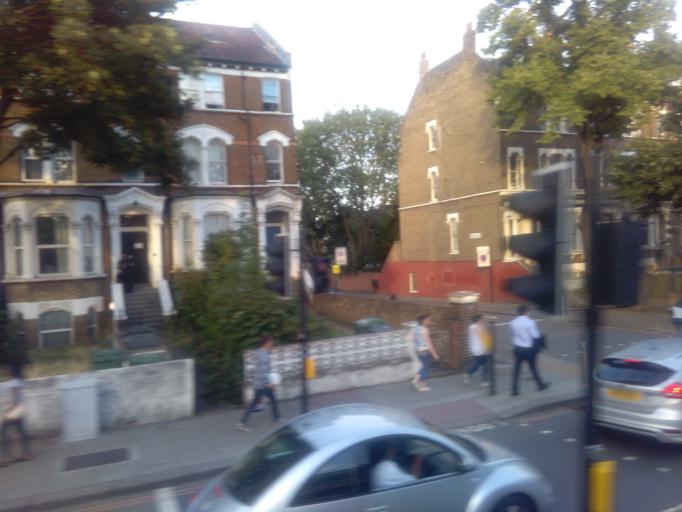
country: GB
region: England
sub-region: Greater London
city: Brixton Hill
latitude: 51.4594
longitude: -0.1152
